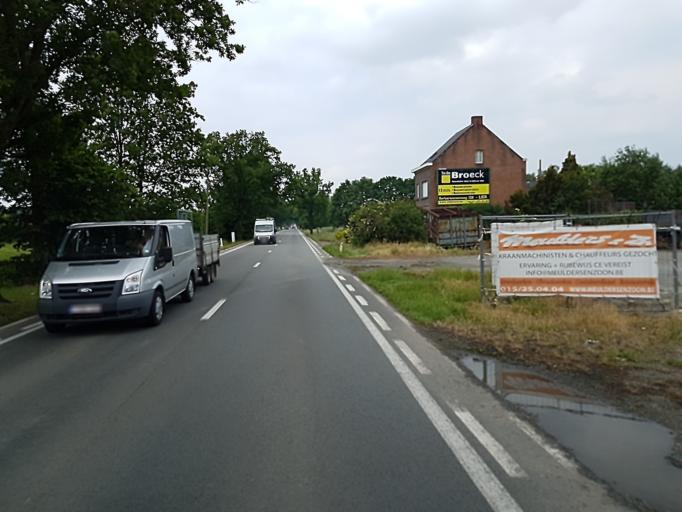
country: BE
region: Flanders
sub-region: Provincie Antwerpen
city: Heist-op-den-Berg
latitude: 51.0741
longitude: 4.6864
